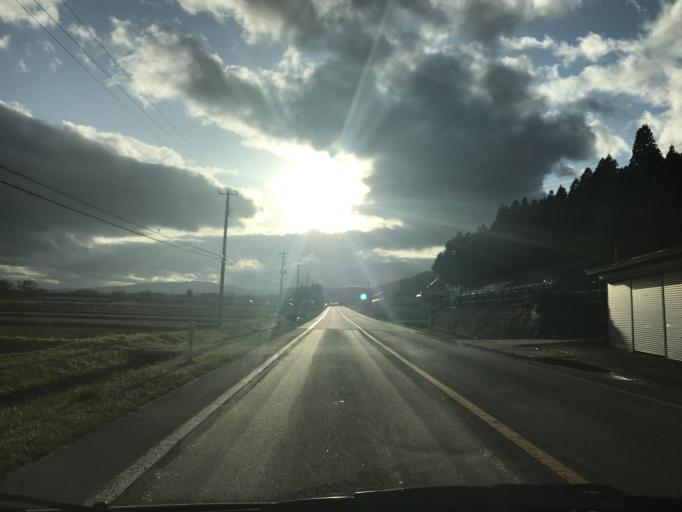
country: JP
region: Iwate
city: Mizusawa
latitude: 39.1527
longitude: 141.0505
